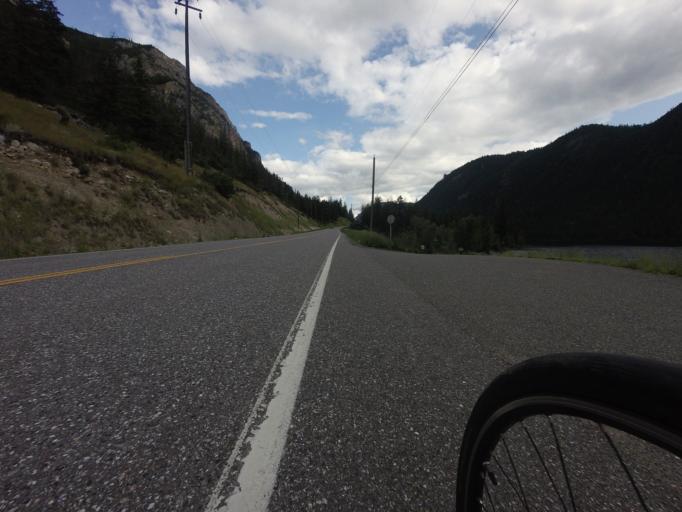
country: CA
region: British Columbia
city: Lillooet
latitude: 50.8617
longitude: -121.7279
